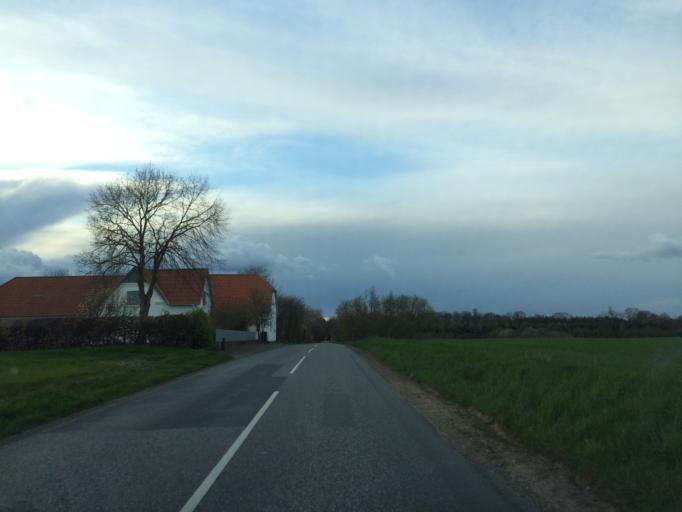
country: DK
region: South Denmark
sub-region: Odense Kommune
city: Bellinge
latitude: 55.2835
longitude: 10.2973
